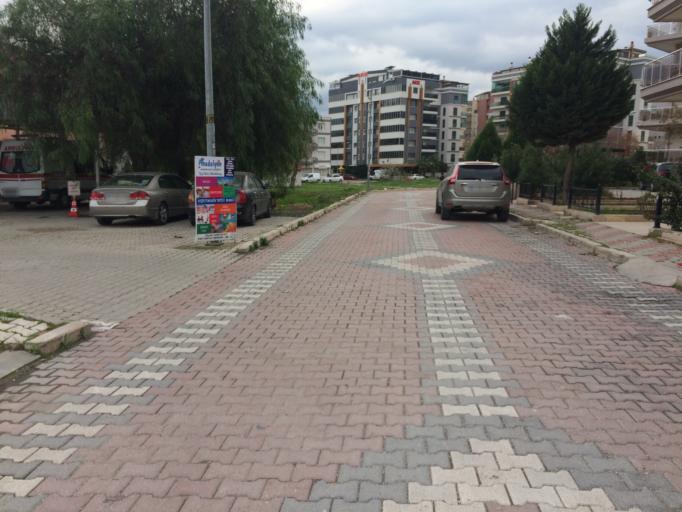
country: TR
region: Izmir
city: Karsiyaka
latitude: 38.4867
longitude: 27.0630
